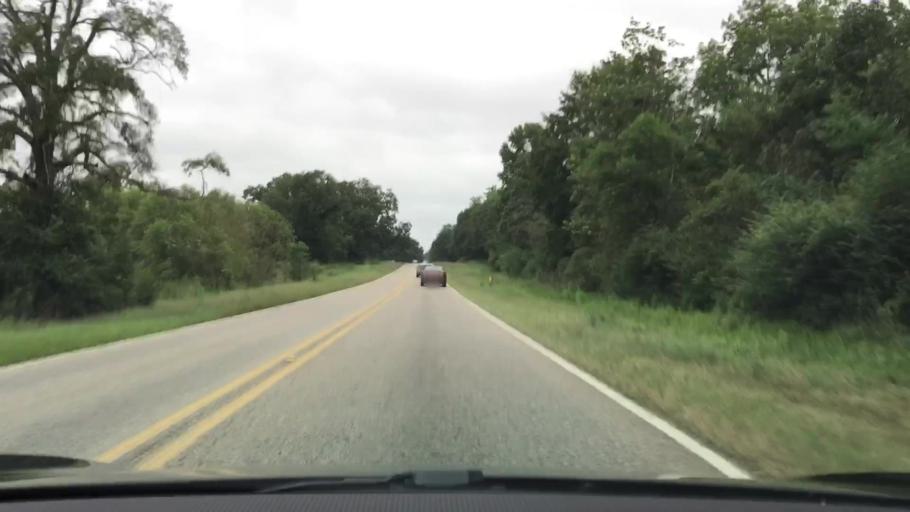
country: US
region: Alabama
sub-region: Geneva County
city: Samson
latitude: 31.1850
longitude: -86.1498
